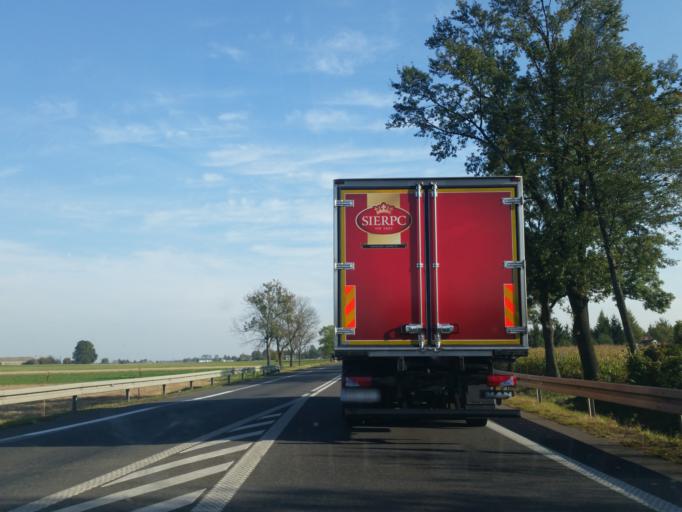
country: PL
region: Masovian Voivodeship
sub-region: Powiat sierpecki
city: Rosciszewo
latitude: 52.8281
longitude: 19.7575
